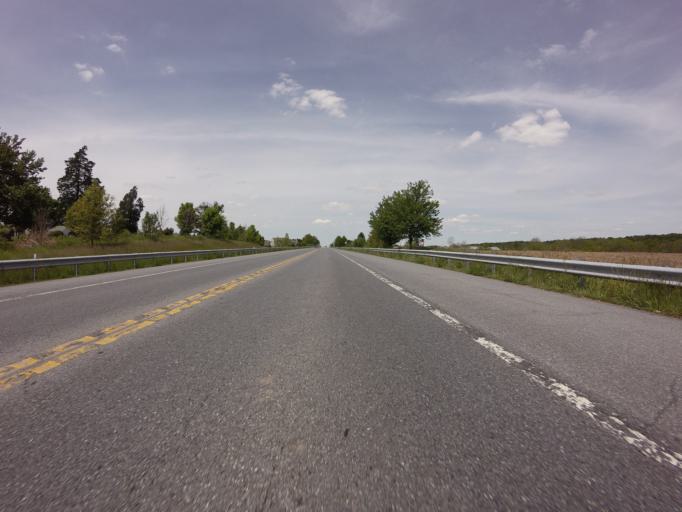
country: US
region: Maryland
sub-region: Frederick County
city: Woodsboro
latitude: 39.5253
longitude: -77.3123
